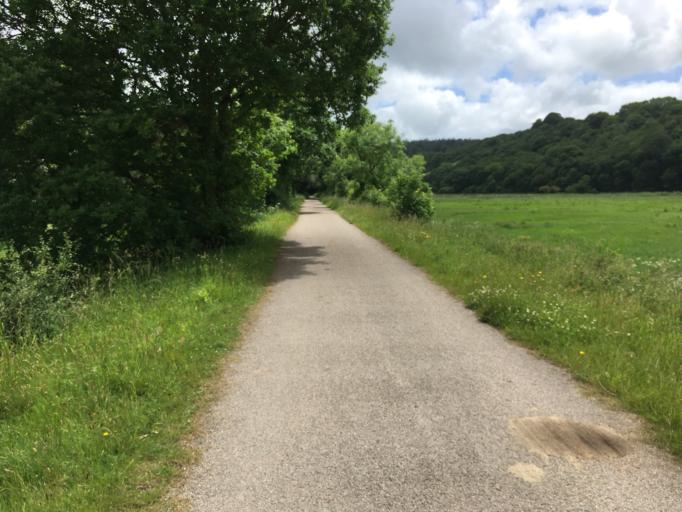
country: GB
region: England
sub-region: Cornwall
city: Wadebridge
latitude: 50.5044
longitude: -4.8160
